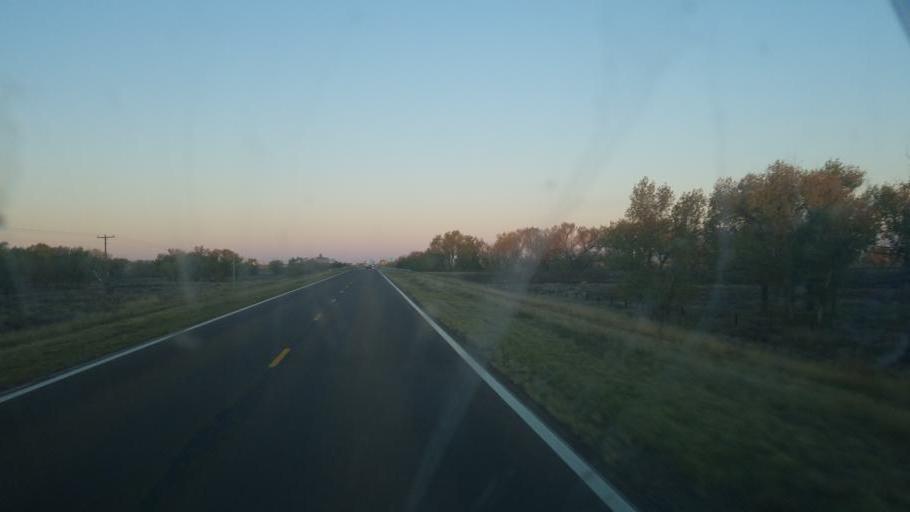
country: US
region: Kansas
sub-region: Wallace County
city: Sharon Springs
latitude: 38.9021
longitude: -101.6911
